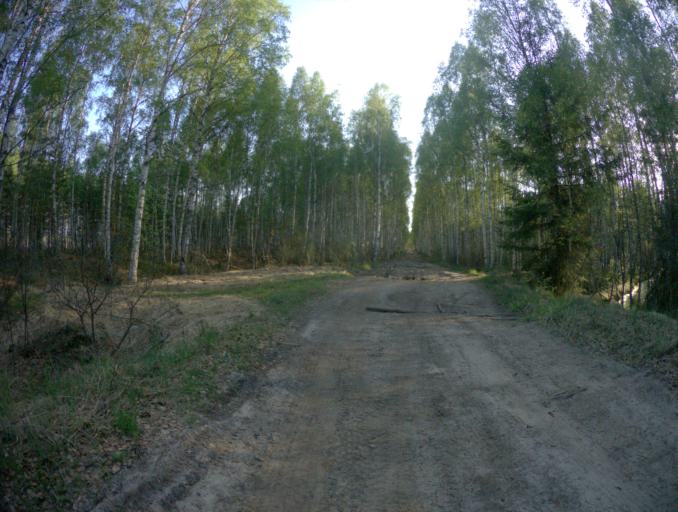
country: RU
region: Vladimir
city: Vyazniki
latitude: 56.3733
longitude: 42.1674
